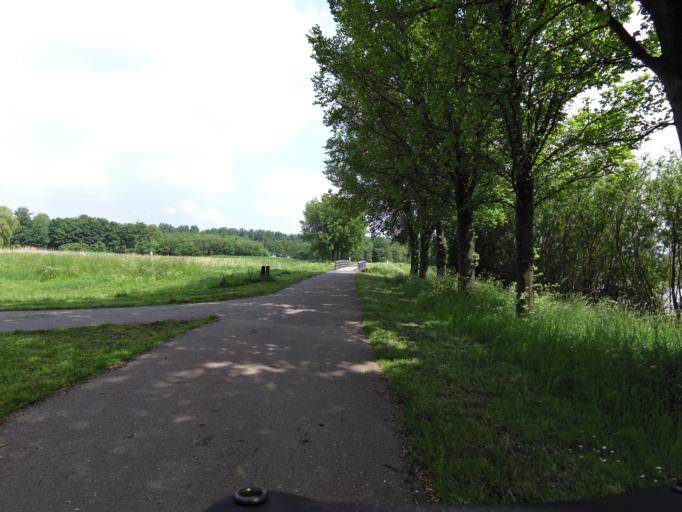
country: NL
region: South Holland
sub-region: Gemeente Spijkenisse
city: Spijkenisse
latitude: 51.8187
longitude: 4.2852
